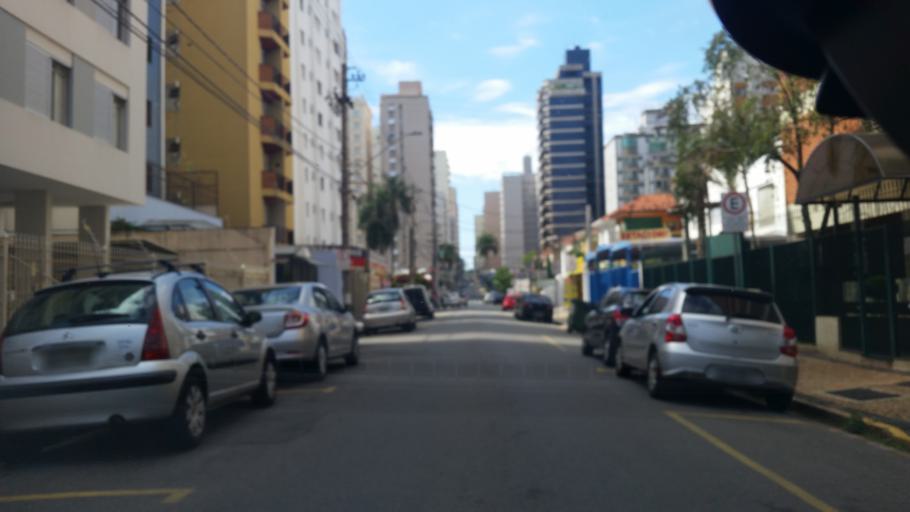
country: BR
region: Sao Paulo
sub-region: Campinas
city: Campinas
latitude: -22.9024
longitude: -47.0557
